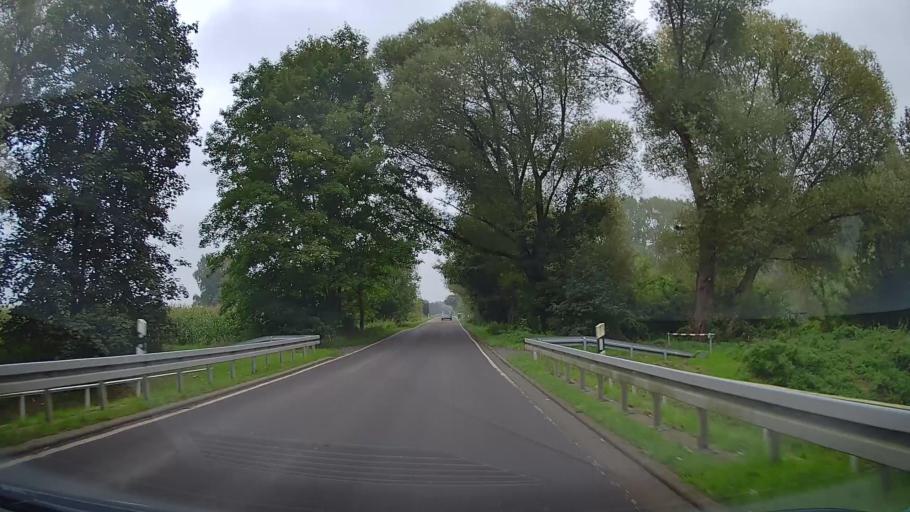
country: DE
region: Mecklenburg-Vorpommern
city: Blowatz
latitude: 53.9648
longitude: 11.5480
